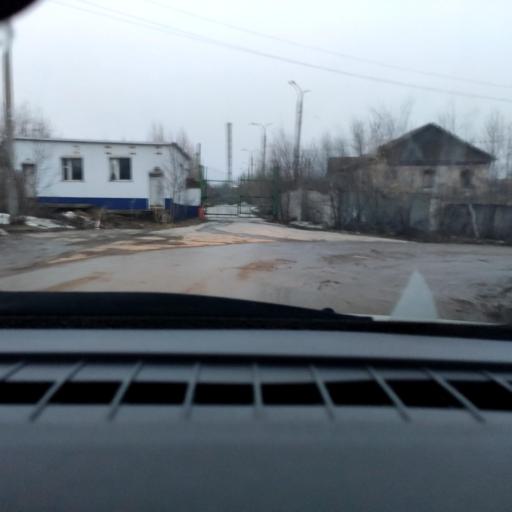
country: RU
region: Samara
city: Volzhskiy
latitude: 53.3470
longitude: 50.2029
